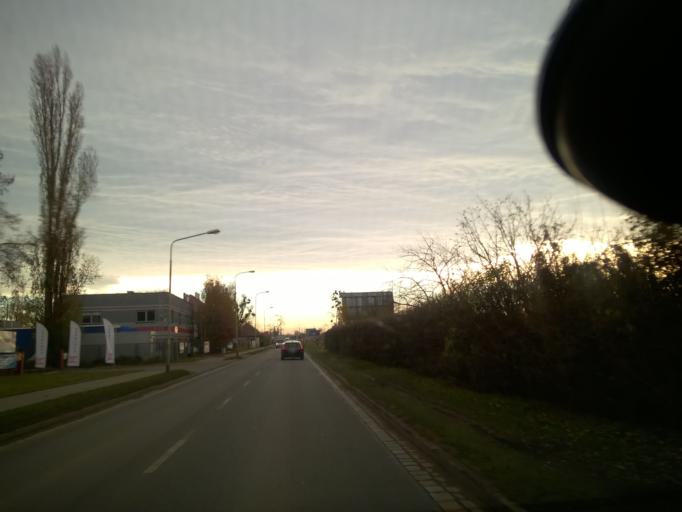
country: PL
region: Lower Silesian Voivodeship
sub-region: Powiat wroclawski
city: Bielany Wroclawskie
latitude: 51.0926
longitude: 16.9499
